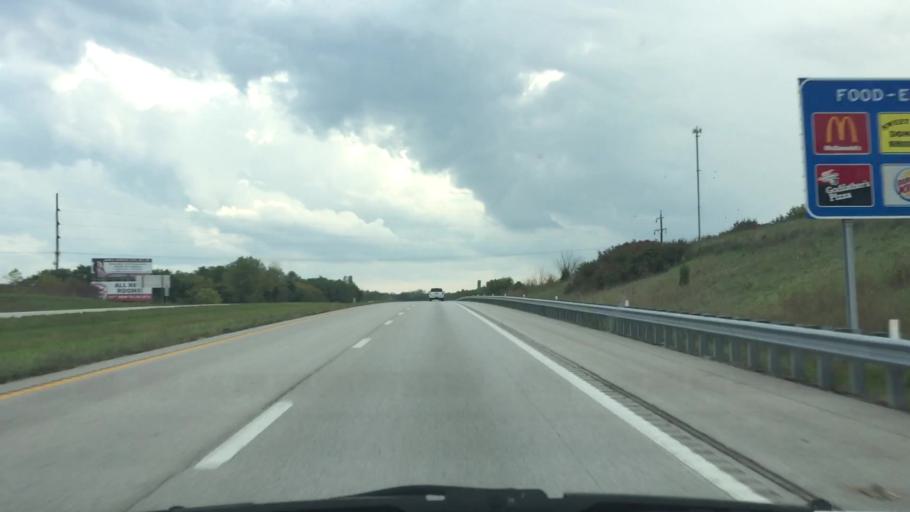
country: US
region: Missouri
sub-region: Clinton County
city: Cameron
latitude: 39.7656
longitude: -94.2161
